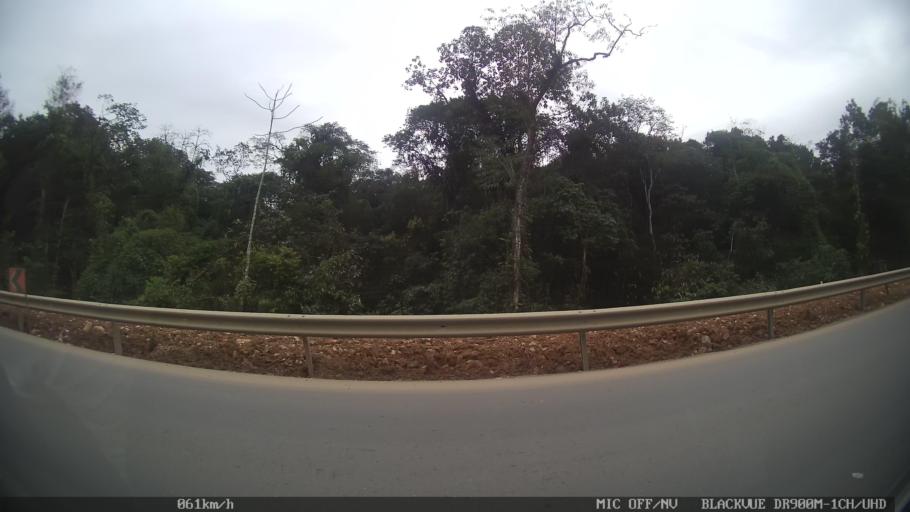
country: BR
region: Santa Catarina
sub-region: Joinville
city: Joinville
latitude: -26.2554
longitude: -48.8942
